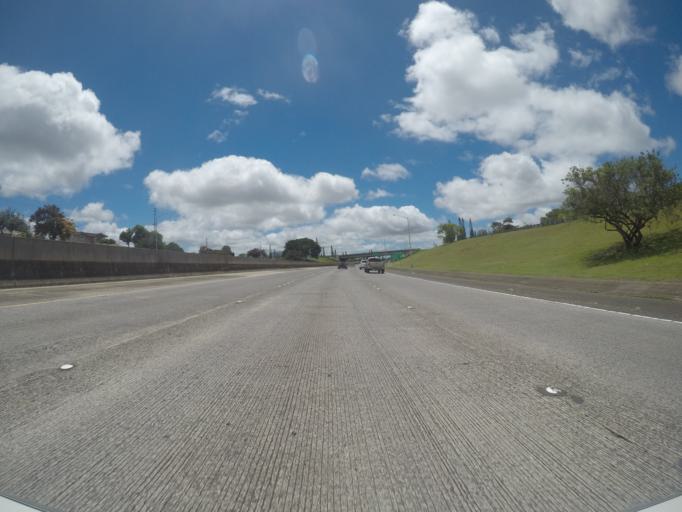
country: US
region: Hawaii
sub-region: Honolulu County
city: Waipi'o Acres
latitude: 21.4639
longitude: -158.0016
